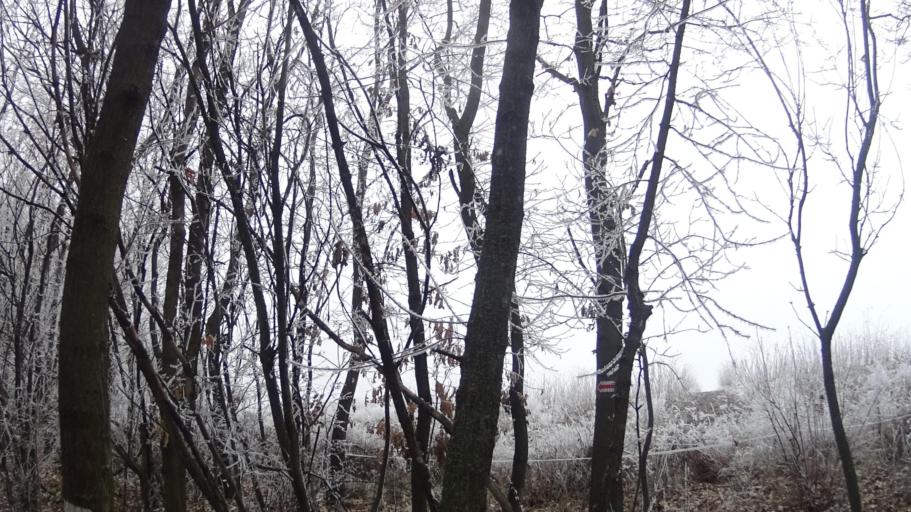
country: HU
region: Pest
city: Kosd
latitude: 47.8030
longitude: 19.1990
